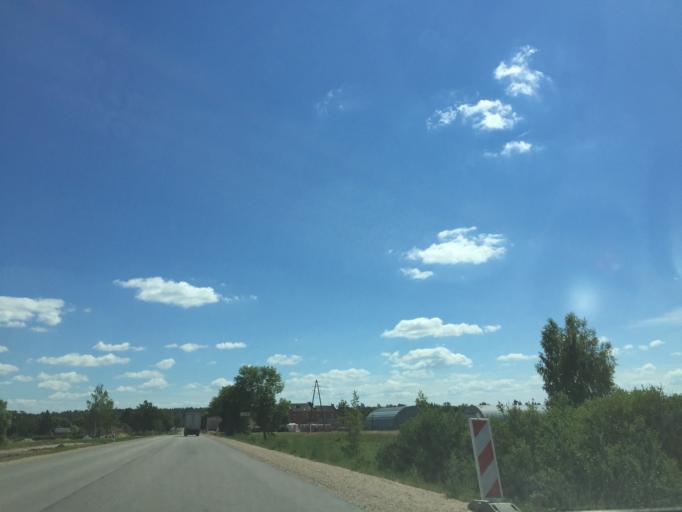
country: LV
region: Vilanu
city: Vilani
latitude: 56.5704
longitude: 26.9219
